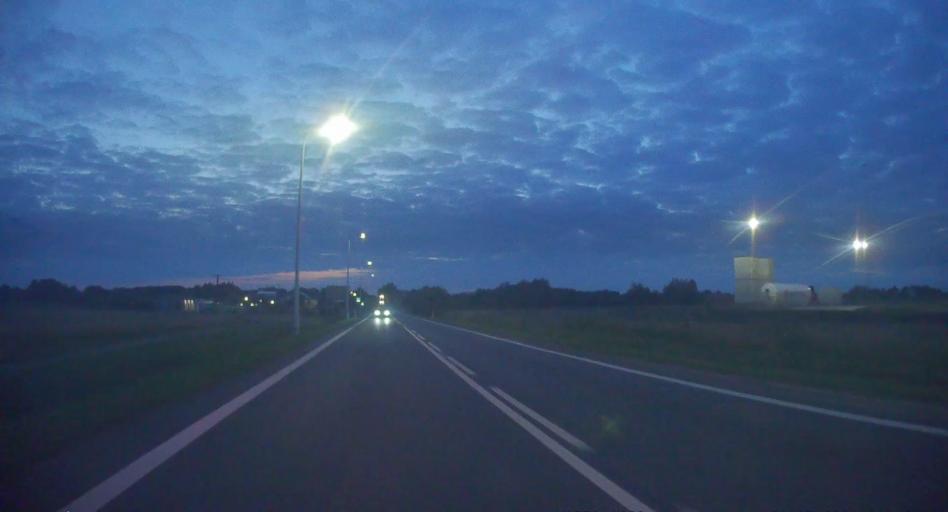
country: PL
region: Silesian Voivodeship
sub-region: Powiat klobucki
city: Kamyk
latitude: 50.8767
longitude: 18.9996
